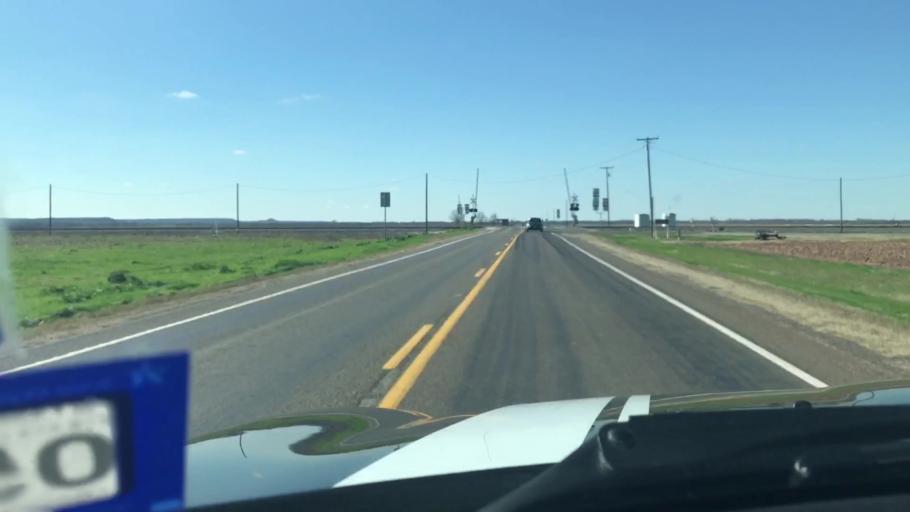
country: US
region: Texas
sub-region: Robertson County
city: Hearne
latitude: 30.8732
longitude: -96.6601
